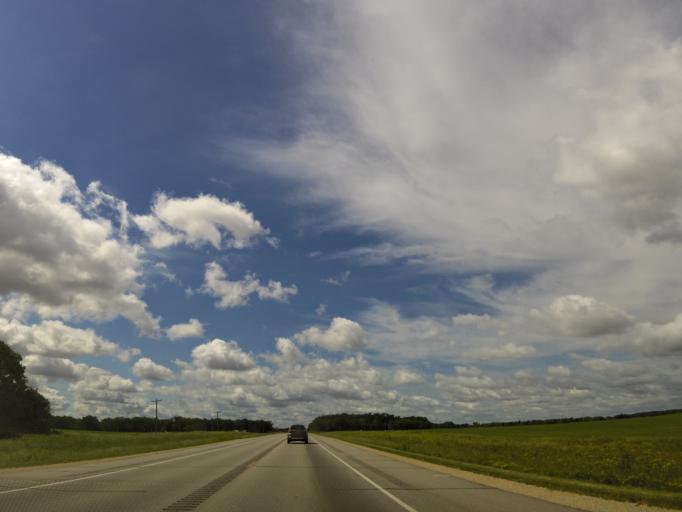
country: US
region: Minnesota
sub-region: Mower County
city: Grand Meadow
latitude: 43.7295
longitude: -92.4793
